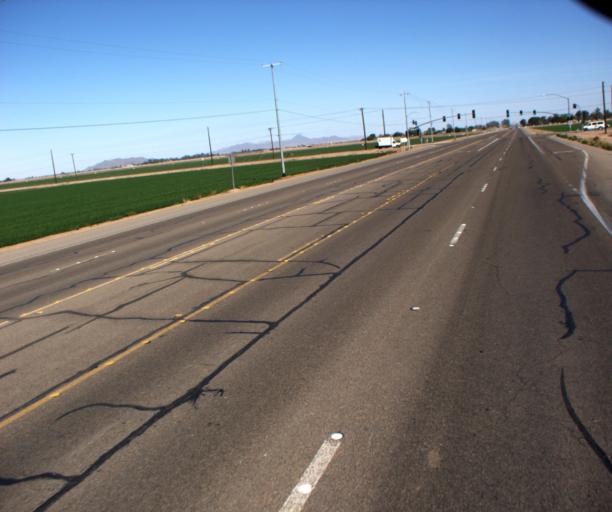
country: US
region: Arizona
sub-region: Yuma County
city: Somerton
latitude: 32.6242
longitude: -114.6498
